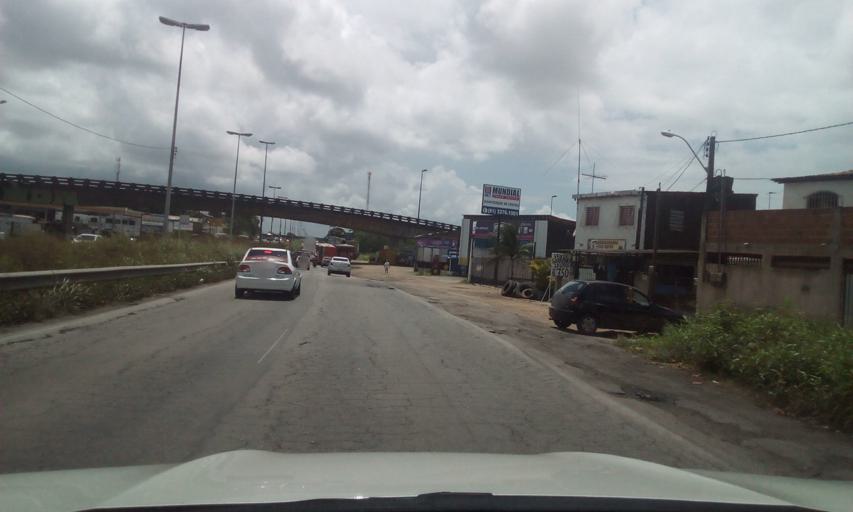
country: BR
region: Pernambuco
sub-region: Recife
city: Recife
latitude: -8.0820
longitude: -34.9432
